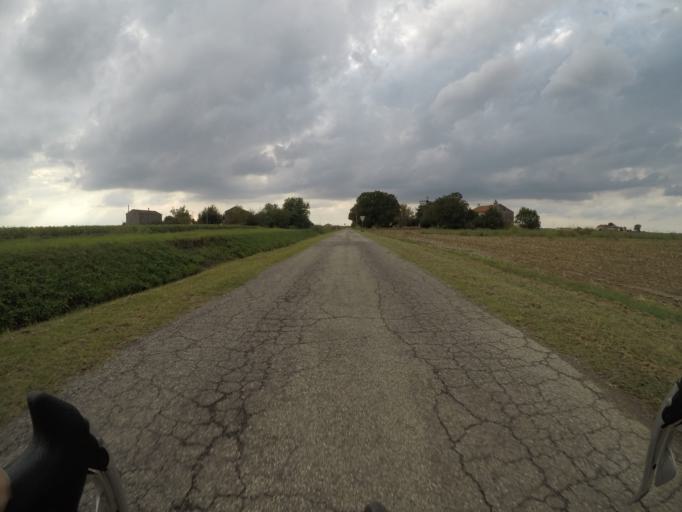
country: IT
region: Veneto
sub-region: Provincia di Rovigo
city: Polesella
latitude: 44.9665
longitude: 11.7255
